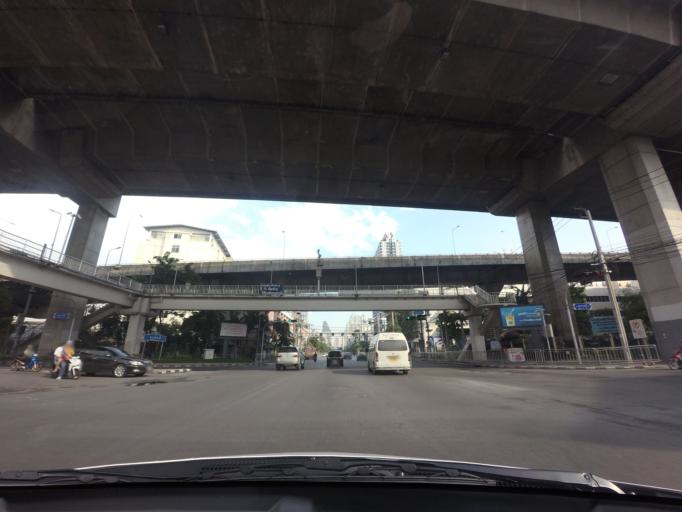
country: TH
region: Bangkok
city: Ratchathewi
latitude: 13.7564
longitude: 100.5236
